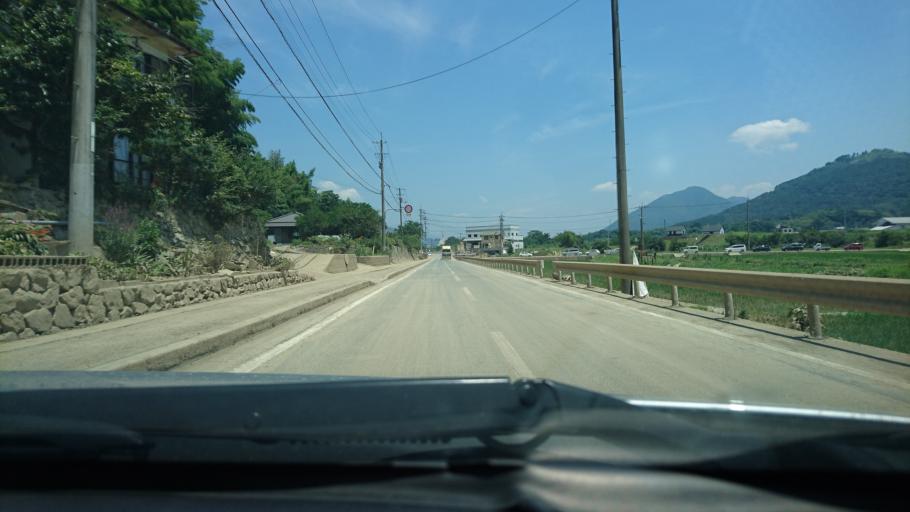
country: JP
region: Ehime
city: Ozu
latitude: 33.5113
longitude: 132.5348
